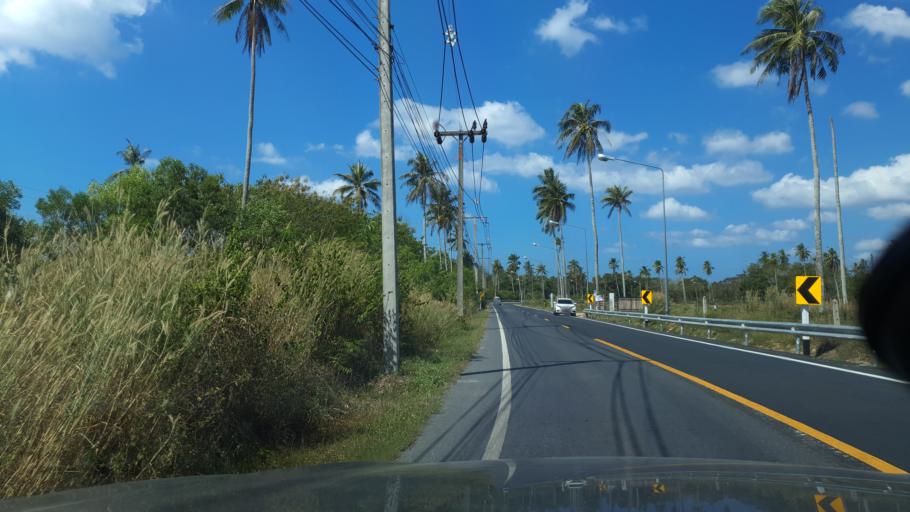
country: TH
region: Phuket
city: Thalang
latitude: 8.1553
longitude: 98.3049
